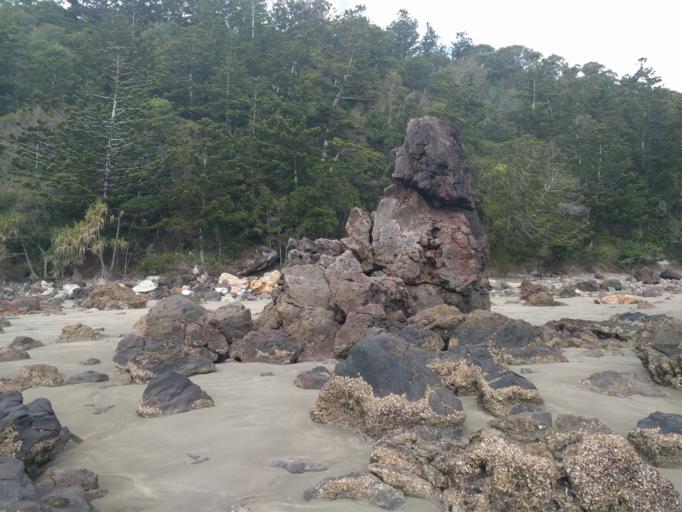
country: AU
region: Queensland
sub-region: Mackay
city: Walkerston
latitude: -20.9181
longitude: 149.0464
